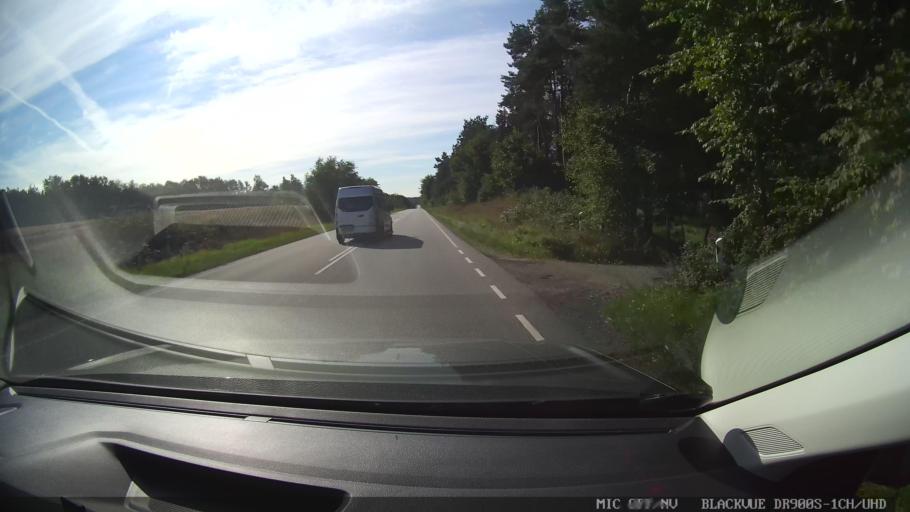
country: DK
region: North Denmark
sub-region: Mariagerfjord Kommune
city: Hadsund
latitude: 56.7481
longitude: 10.0739
